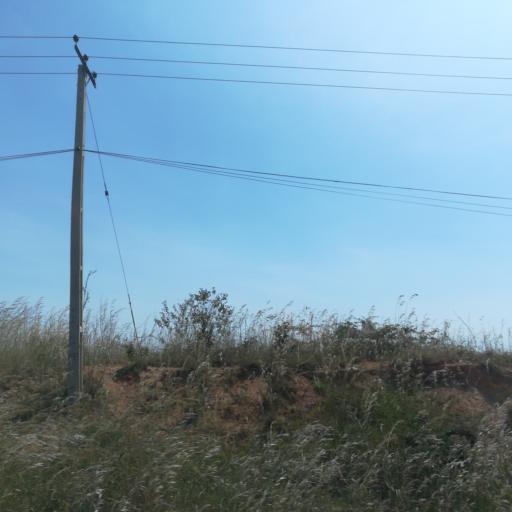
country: NG
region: Plateau
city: Bukuru
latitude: 9.8468
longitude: 8.9177
